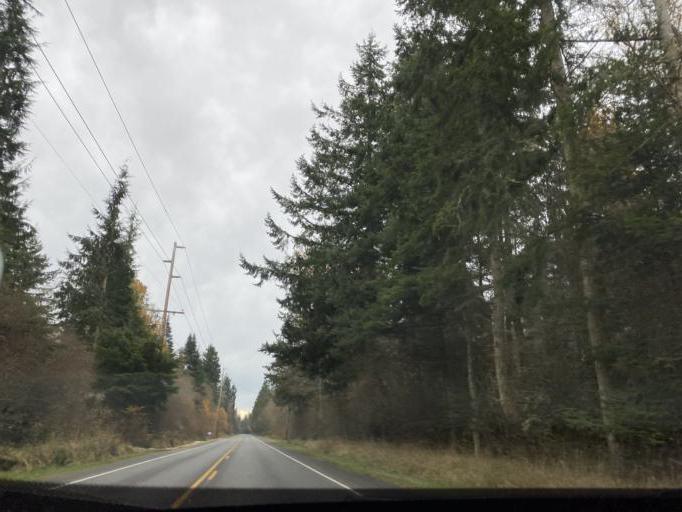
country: US
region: Washington
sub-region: Island County
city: Freeland
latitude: 48.0428
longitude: -122.5899
